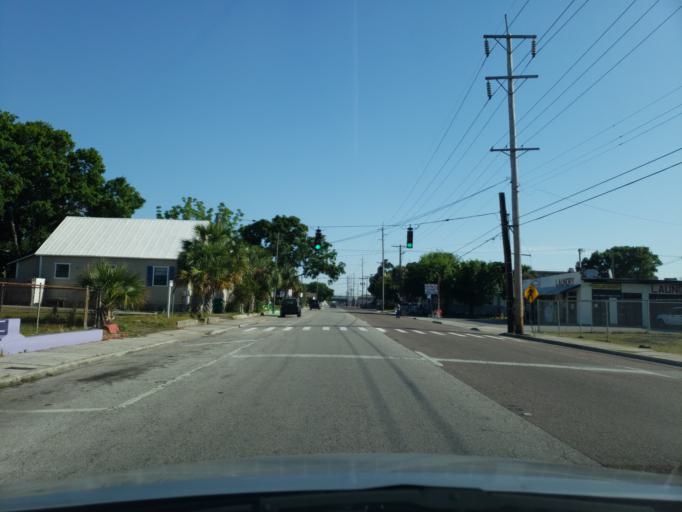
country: US
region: Florida
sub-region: Hillsborough County
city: Tampa
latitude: 27.9608
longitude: -82.4849
